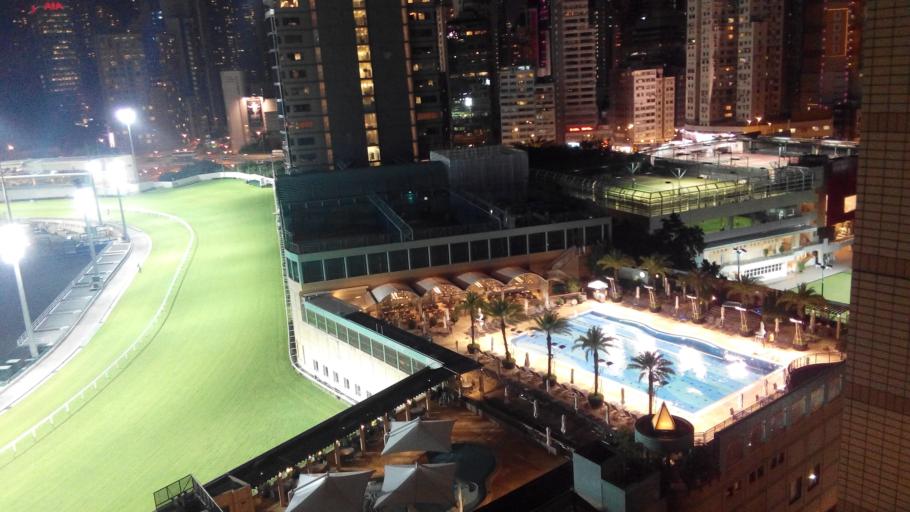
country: HK
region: Wanchai
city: Wan Chai
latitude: 22.2744
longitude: 114.1830
